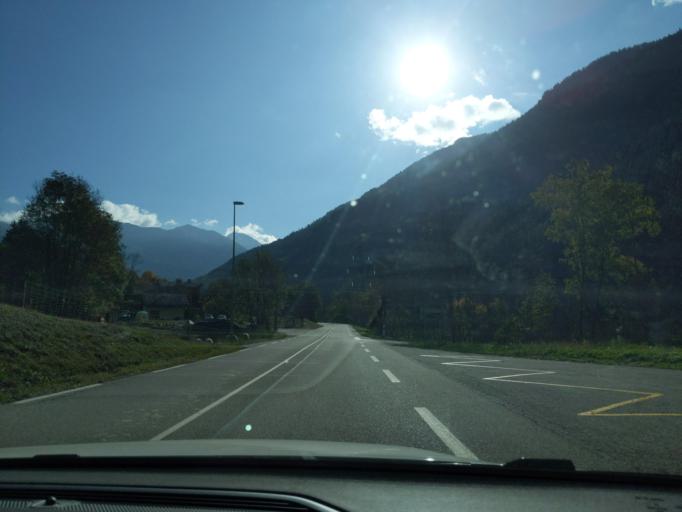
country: FR
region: Rhone-Alpes
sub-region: Departement de la Savoie
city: Seez
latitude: 45.6149
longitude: 6.8223
